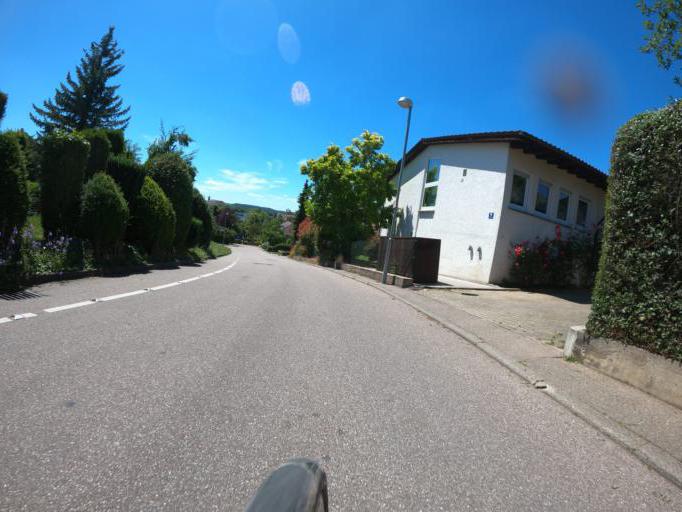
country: DE
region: Baden-Wuerttemberg
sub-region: Regierungsbezirk Stuttgart
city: Vaihingen an der Enz
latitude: 48.9387
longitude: 8.9643
